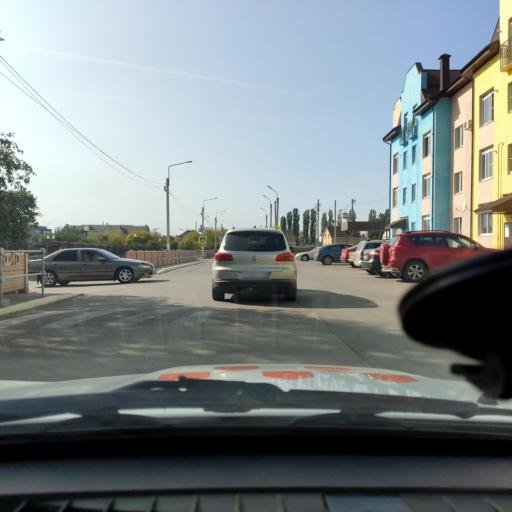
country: RU
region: Voronezj
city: Novaya Usman'
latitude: 51.6540
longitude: 39.3334
